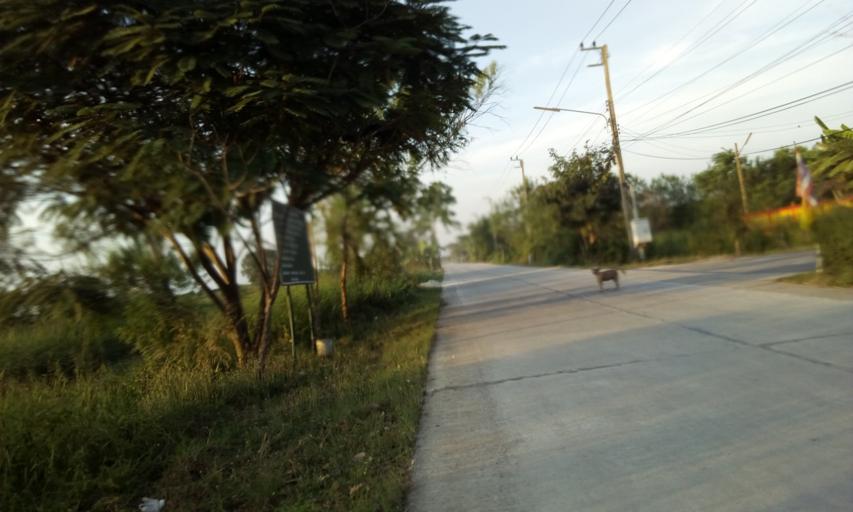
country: TH
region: Pathum Thani
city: Nong Suea
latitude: 14.0377
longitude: 100.8663
